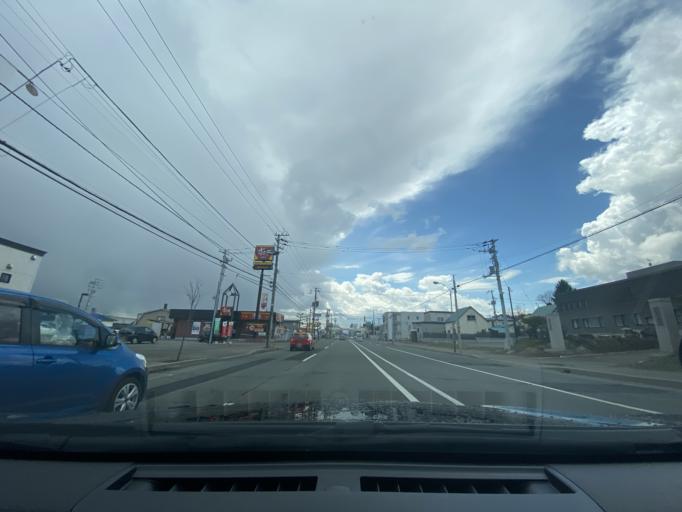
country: JP
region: Hokkaido
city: Kitami
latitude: 43.8138
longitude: 143.9048
